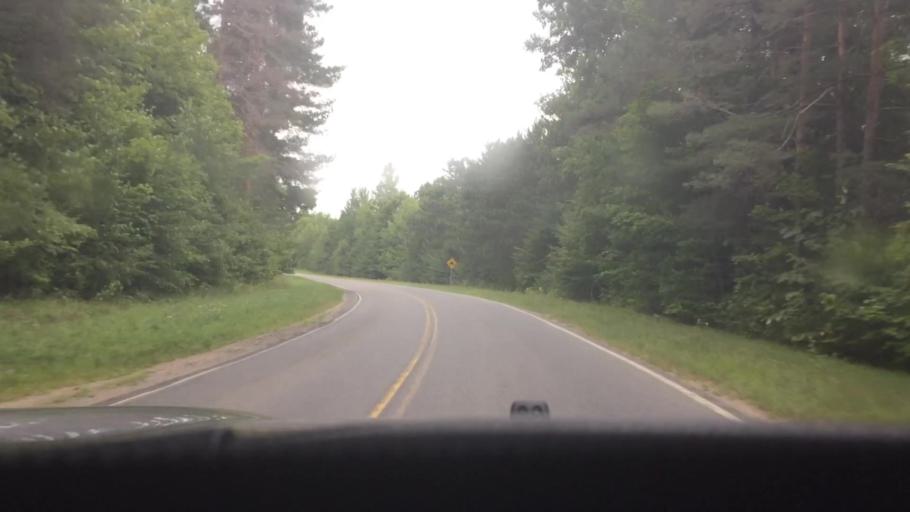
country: US
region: New York
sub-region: St. Lawrence County
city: Hannawa Falls
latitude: 44.6025
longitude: -74.8844
